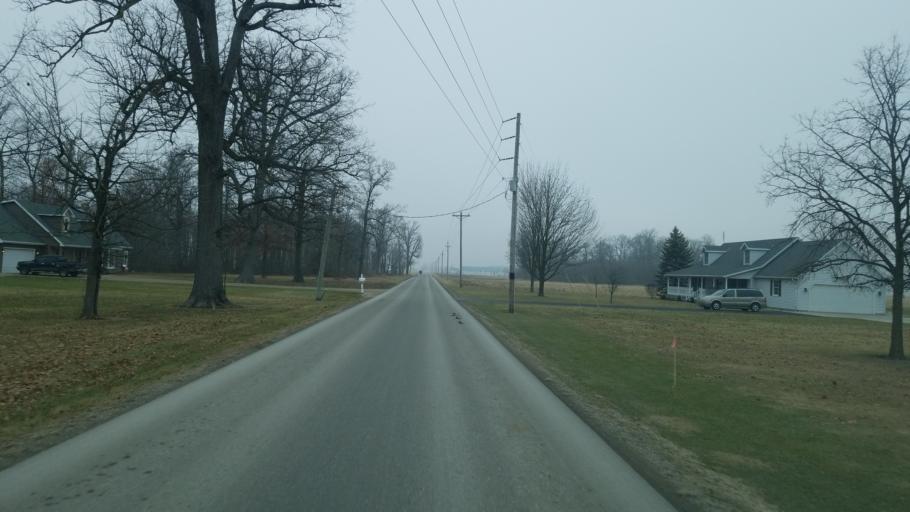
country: US
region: Indiana
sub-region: Adams County
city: Berne
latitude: 40.6865
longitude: -84.9944
